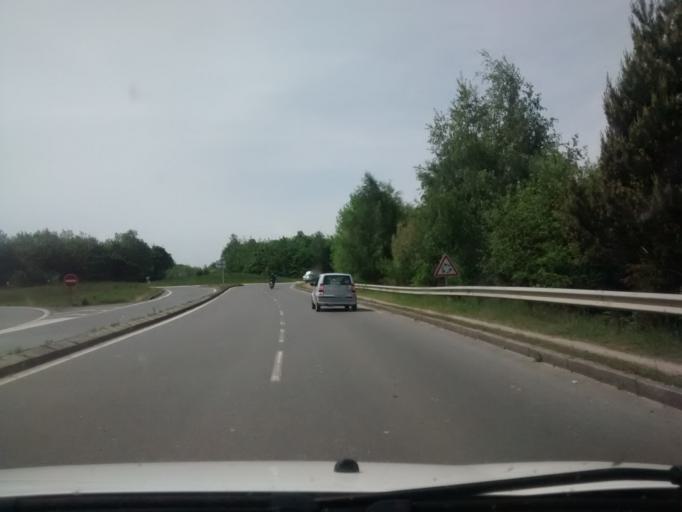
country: FR
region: Brittany
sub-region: Departement d'Ille-et-Vilaine
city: La Chapelle-des-Fougeretz
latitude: 48.2040
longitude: -1.7315
